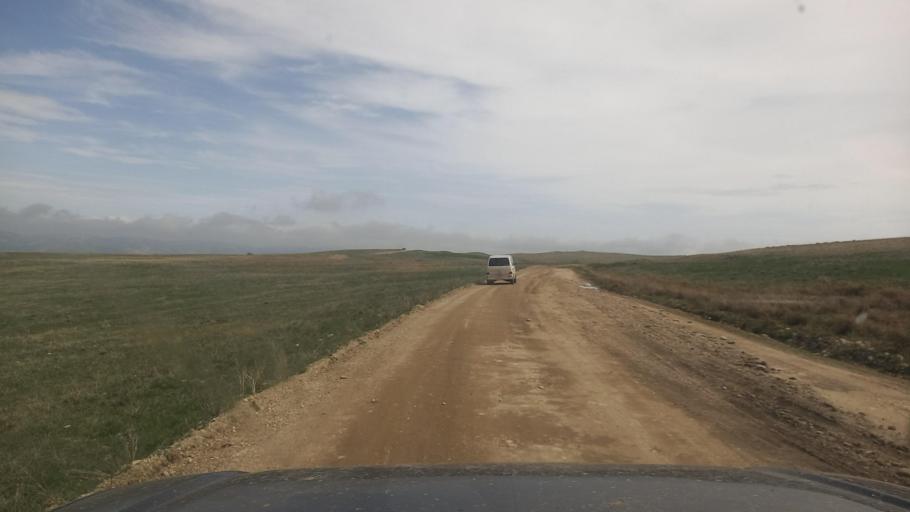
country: RU
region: Stavropol'skiy
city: Kislovodsk
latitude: 43.7642
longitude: 42.8109
